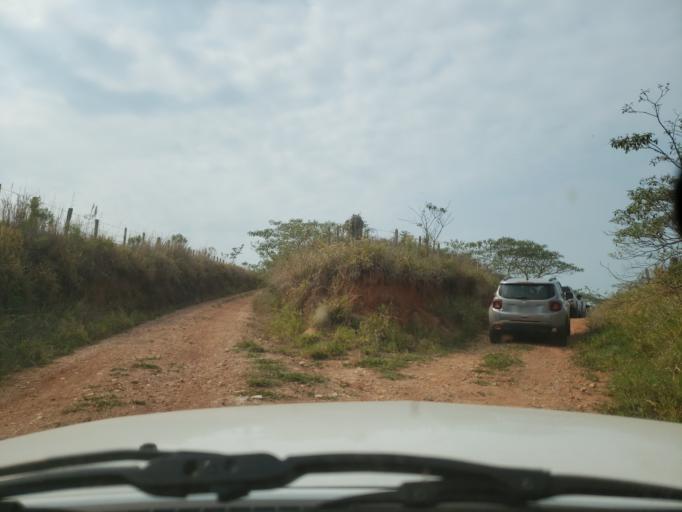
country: BR
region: Minas Gerais
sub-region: Jacutinga
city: Jacutinga
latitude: -22.3408
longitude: -46.5857
